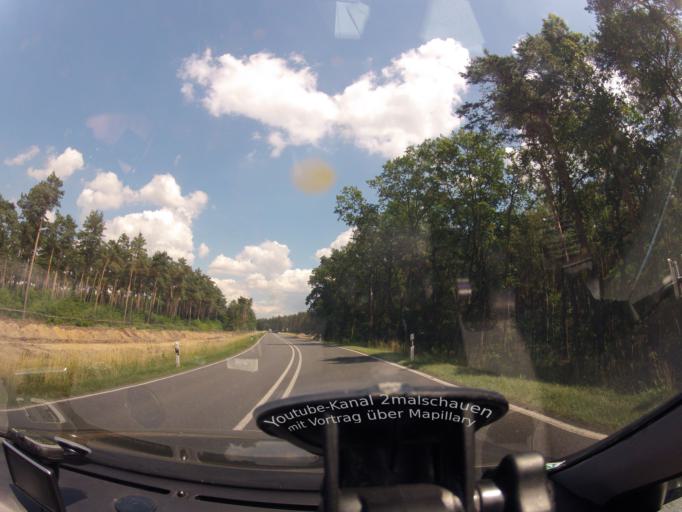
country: DE
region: Saxony
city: Mockrehna
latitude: 51.5245
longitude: 12.8771
